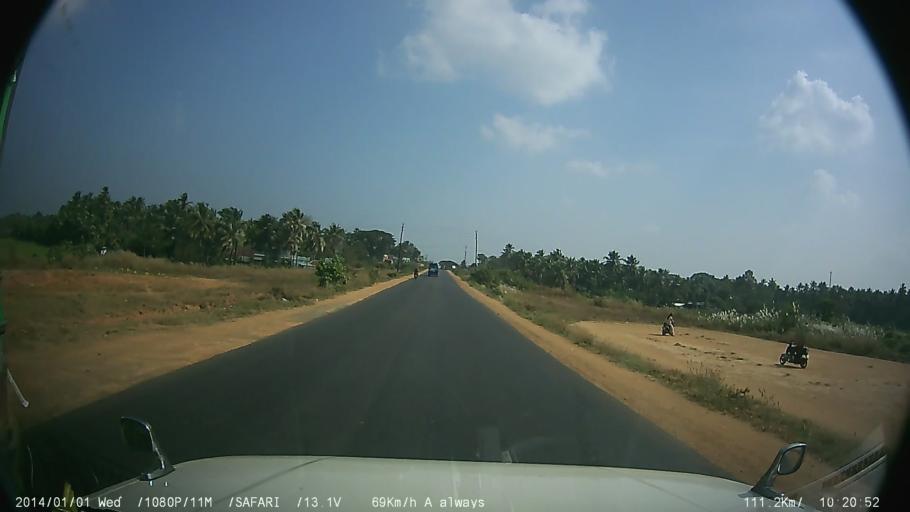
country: IN
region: Kerala
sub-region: Thrissur District
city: Chelakara
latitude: 10.5914
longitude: 76.4786
